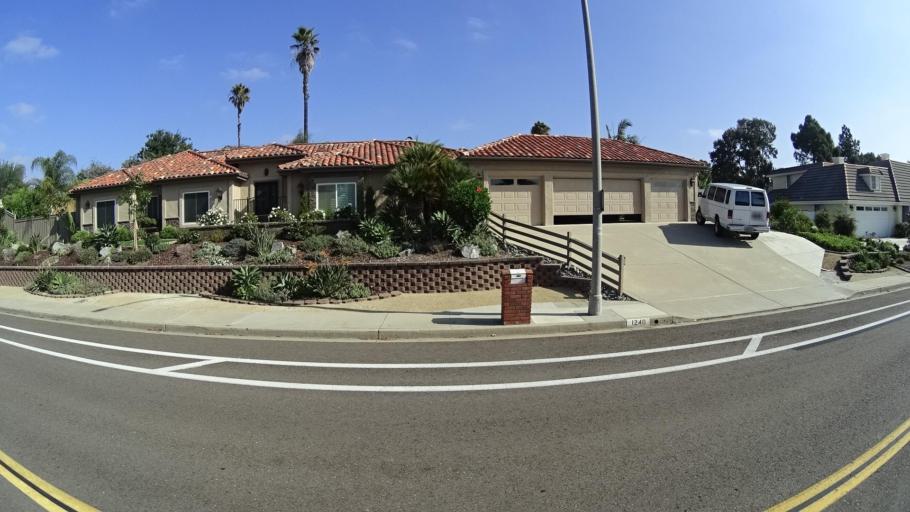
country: US
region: California
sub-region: San Diego County
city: Vista
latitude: 33.1717
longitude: -117.2344
